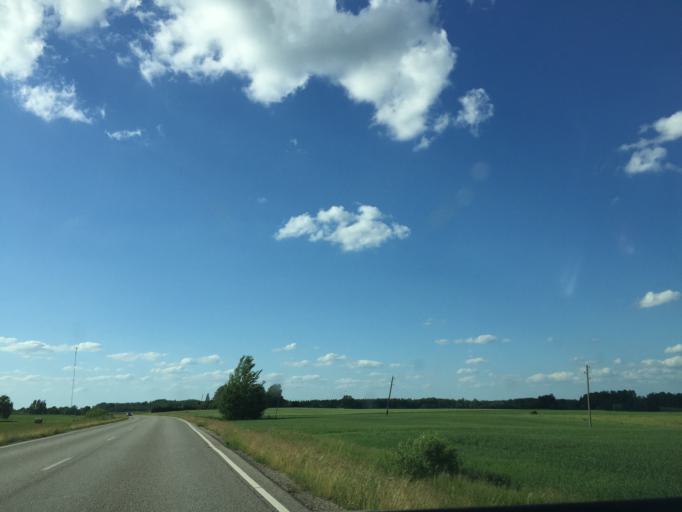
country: LV
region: Kandava
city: Kandava
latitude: 56.9200
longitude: 22.8226
